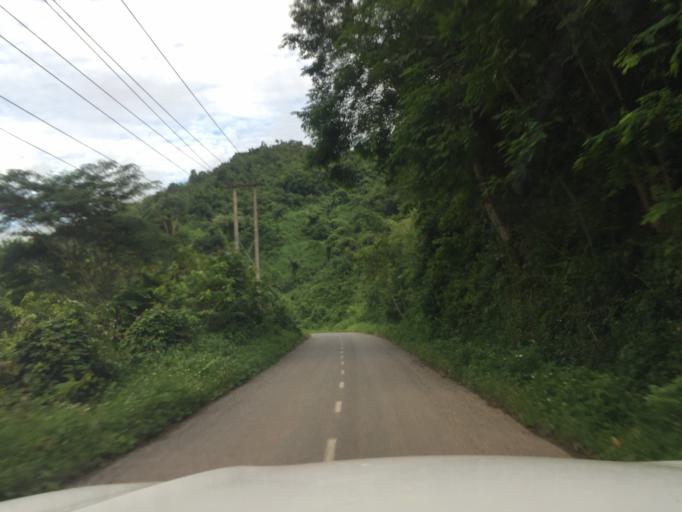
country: LA
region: Phongsali
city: Khoa
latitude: 21.1015
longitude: 102.2798
